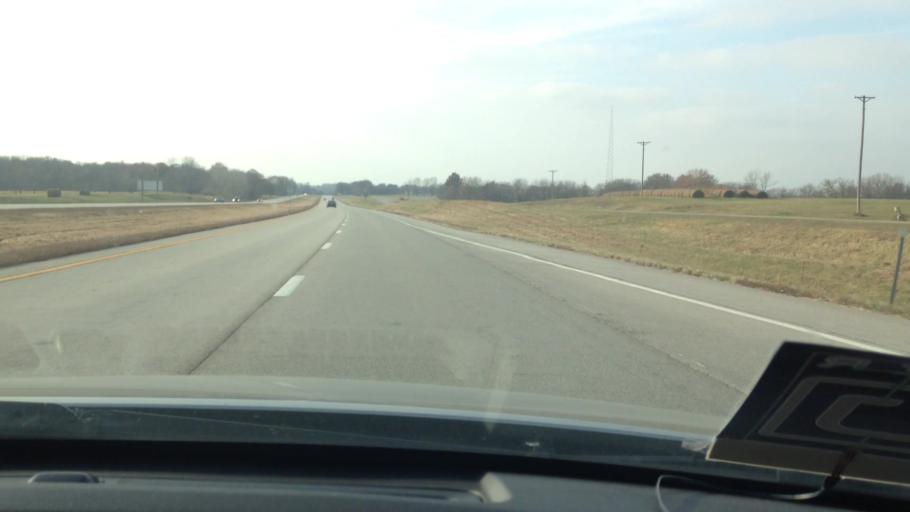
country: US
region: Missouri
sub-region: Cass County
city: Garden City
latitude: 38.5028
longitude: -94.0766
